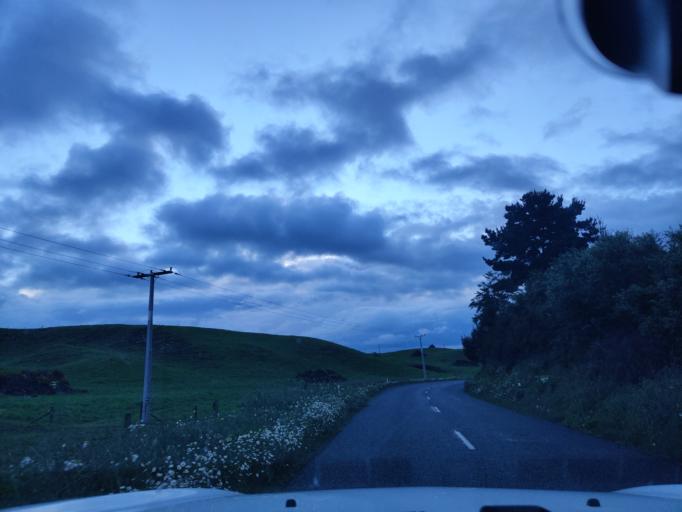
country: NZ
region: Waikato
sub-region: South Waikato District
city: Tokoroa
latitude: -38.1794
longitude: 175.7802
